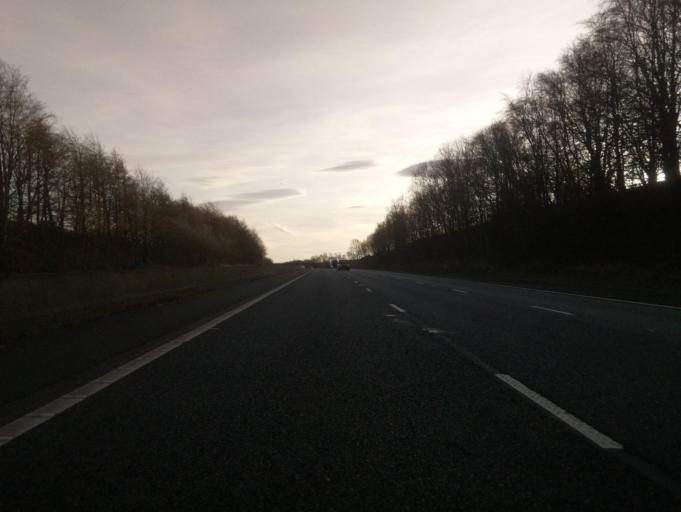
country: GB
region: England
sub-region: Cumbria
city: Scotby
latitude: 54.8306
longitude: -2.8895
